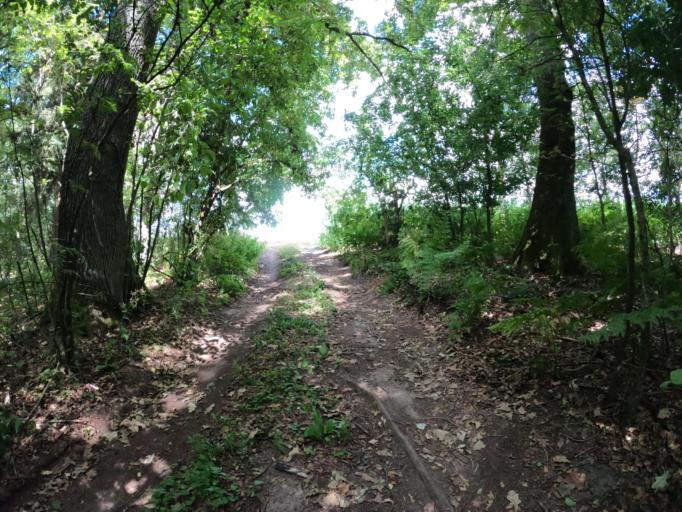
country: PL
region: West Pomeranian Voivodeship
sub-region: Powiat swidwinski
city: Swidwin
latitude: 53.7551
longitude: 15.8195
